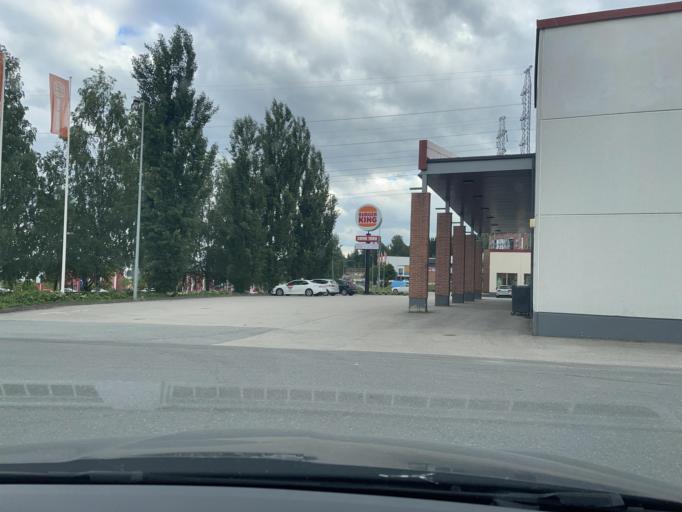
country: FI
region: Central Finland
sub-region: Jyvaeskylae
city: Jyvaeskylae
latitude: 62.2177
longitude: 25.7186
